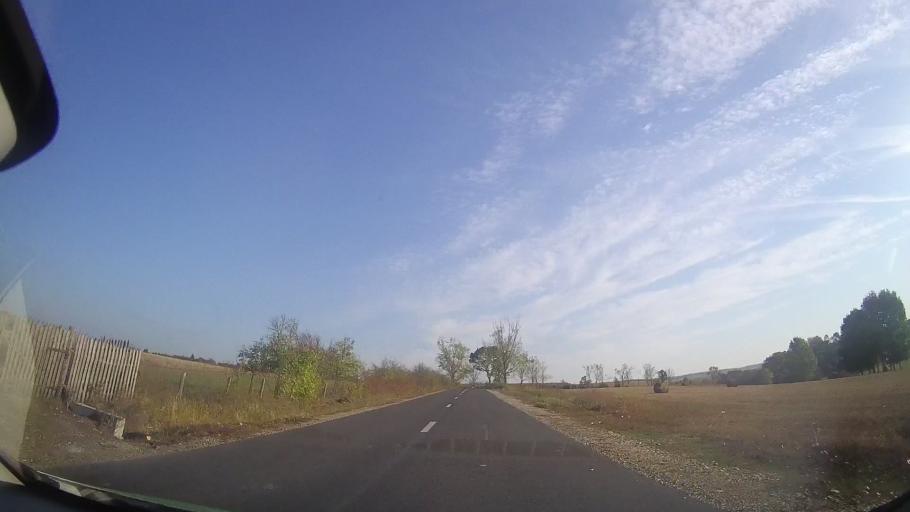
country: RO
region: Timis
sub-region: Comuna Masloc
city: Masloc
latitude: 45.9759
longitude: 21.4974
